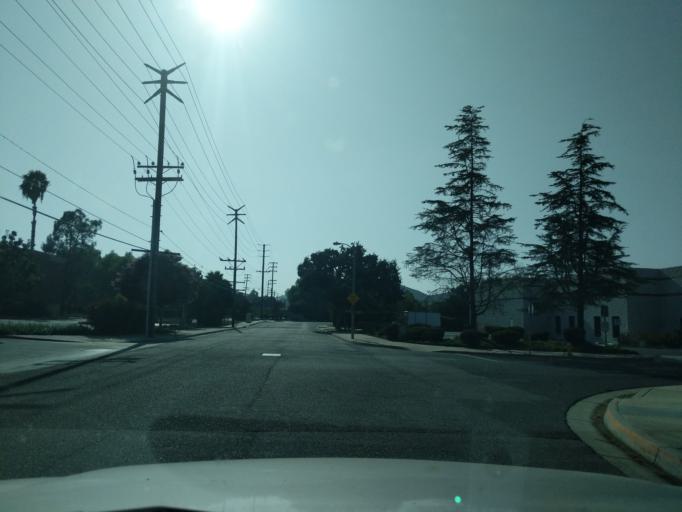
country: US
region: California
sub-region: Ventura County
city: Simi Valley
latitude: 34.2740
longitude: -118.7992
